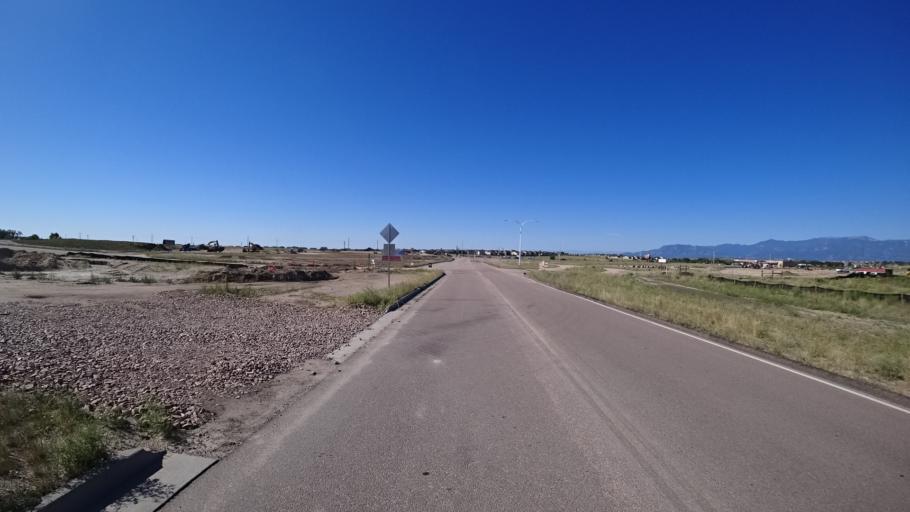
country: US
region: Colorado
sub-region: El Paso County
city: Black Forest
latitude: 38.9438
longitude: -104.6778
